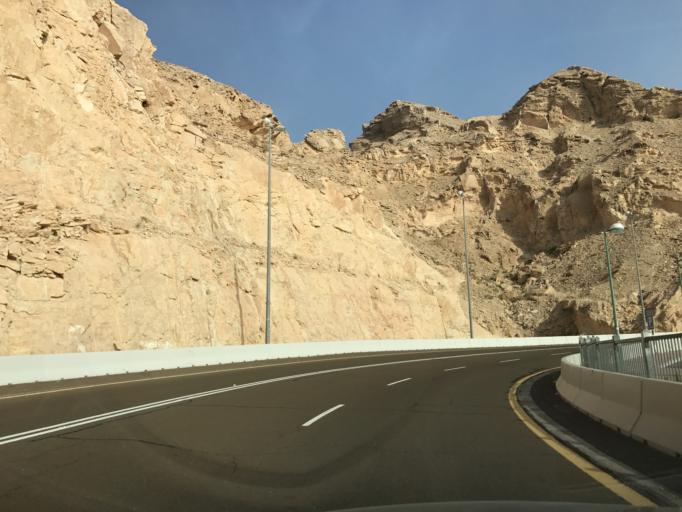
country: AE
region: Abu Dhabi
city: Al Ain
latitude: 24.0987
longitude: 55.7591
